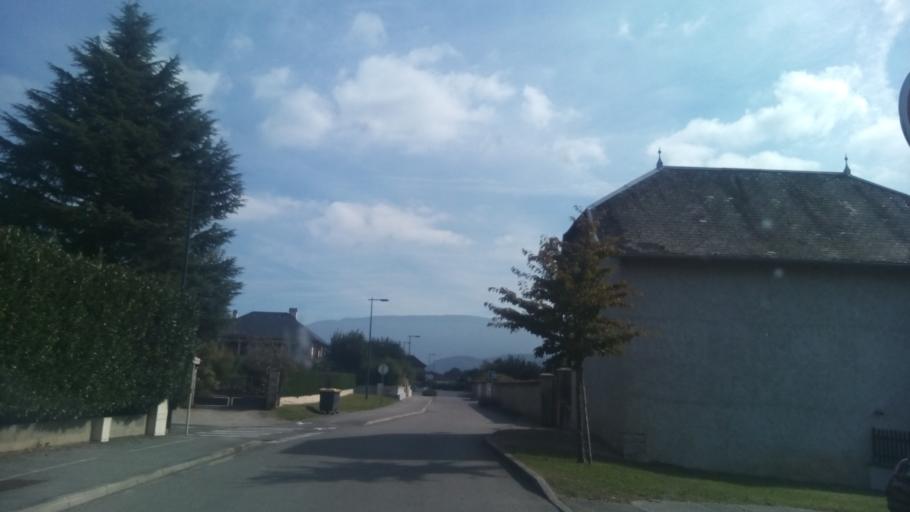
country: FR
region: Rhone-Alpes
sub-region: Departement de la Savoie
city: Le Pont-de-Beauvoisin
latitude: 45.5361
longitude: 5.6855
